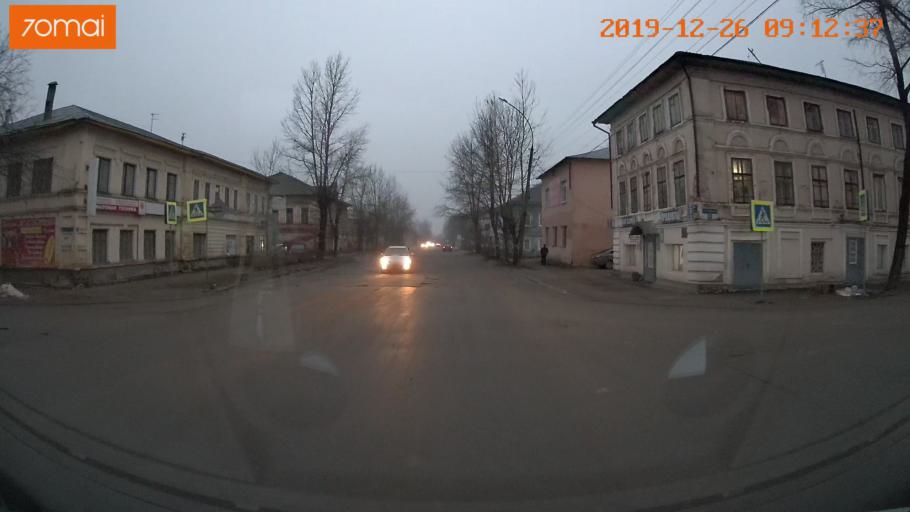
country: RU
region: Vologda
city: Gryazovets
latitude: 58.8821
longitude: 40.2535
